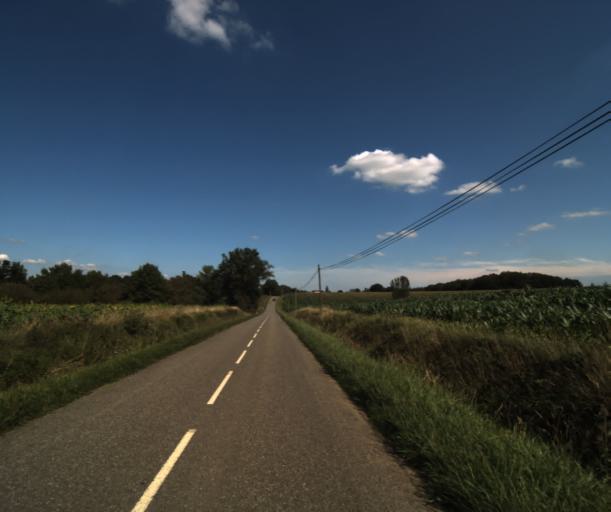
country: FR
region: Midi-Pyrenees
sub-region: Departement de la Haute-Garonne
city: Fonsorbes
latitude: 43.5031
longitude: 1.2118
